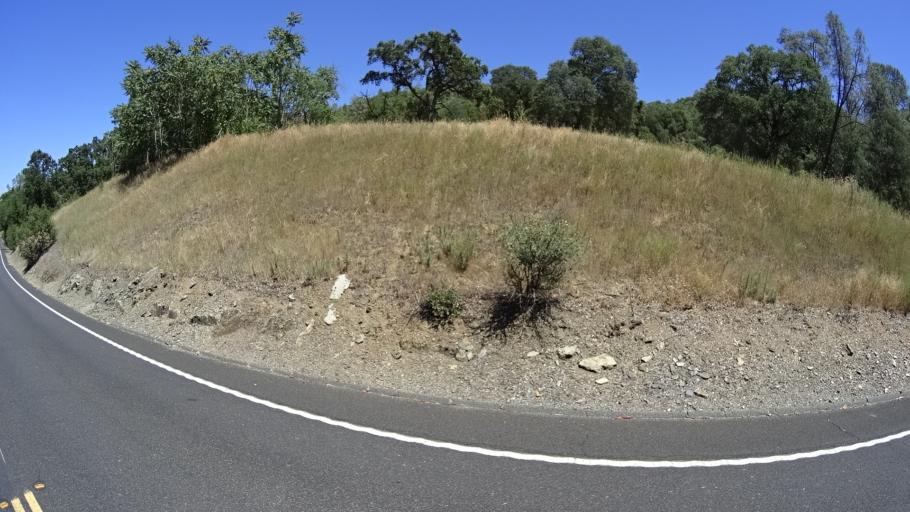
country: US
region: California
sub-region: Calaveras County
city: San Andreas
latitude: 38.2681
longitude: -120.7157
